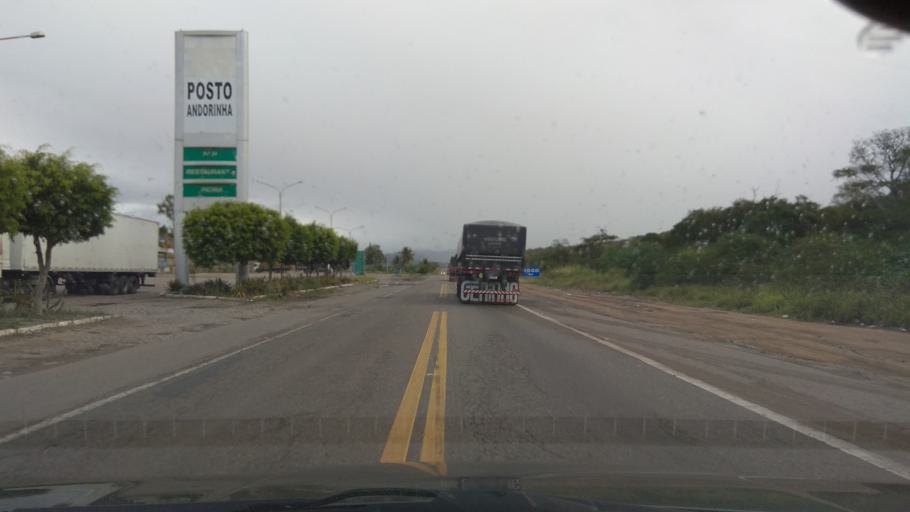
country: BR
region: Bahia
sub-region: Amargosa
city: Amargosa
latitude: -12.9052
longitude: -39.8620
